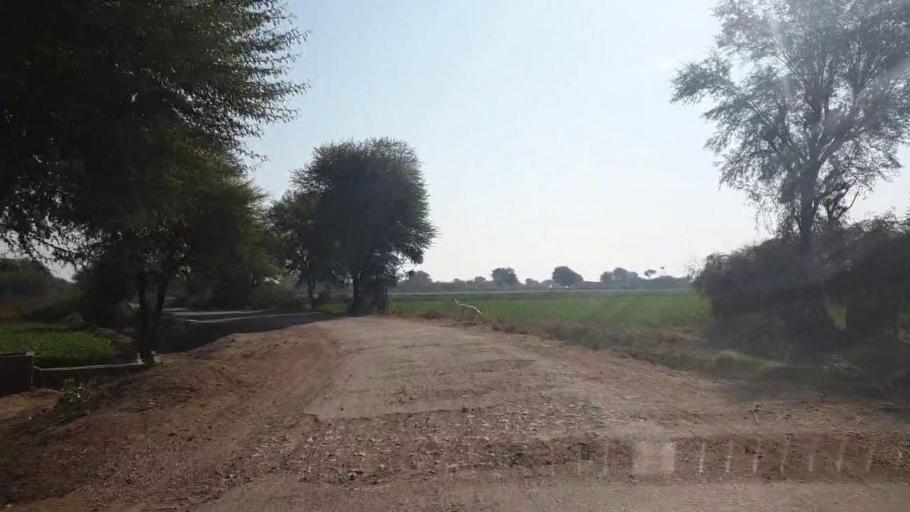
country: PK
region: Sindh
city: Shahpur Chakar
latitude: 26.0820
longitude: 68.6025
